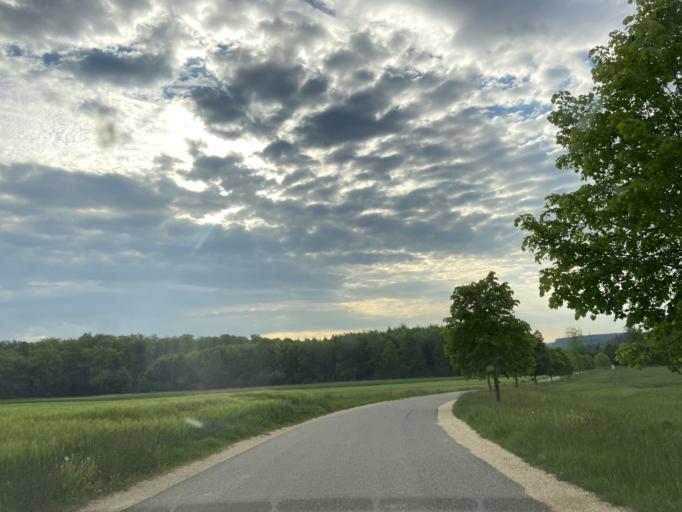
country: DE
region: Baden-Wuerttemberg
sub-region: Tuebingen Region
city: Scheer
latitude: 48.0983
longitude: 9.3121
